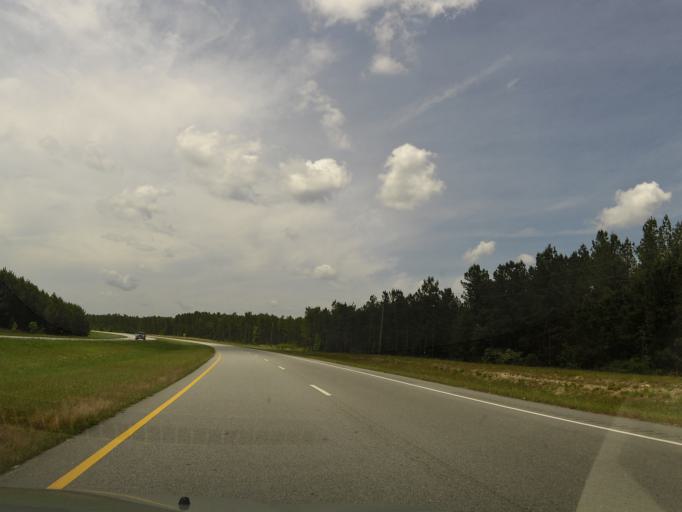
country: US
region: Georgia
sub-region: Jefferson County
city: Wadley
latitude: 32.7712
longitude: -82.3829
